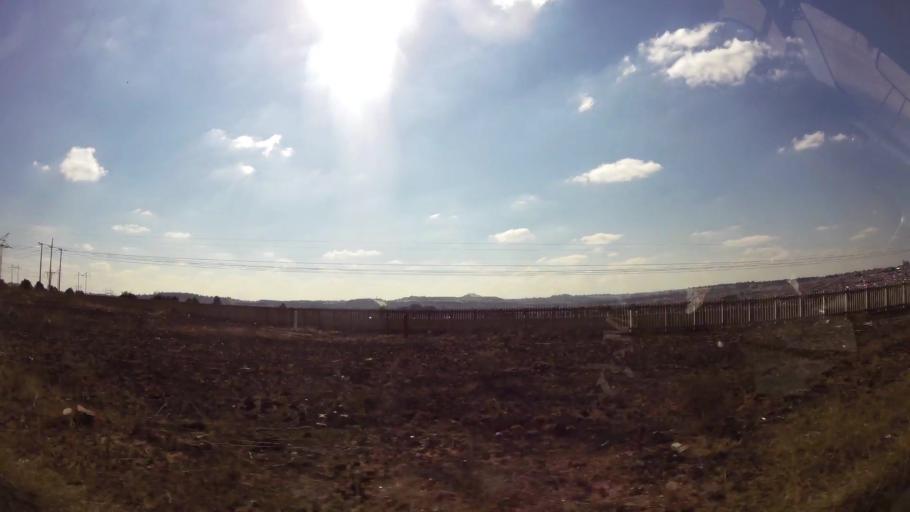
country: ZA
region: Gauteng
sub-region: West Rand District Municipality
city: Randfontein
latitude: -26.1630
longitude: 27.7565
